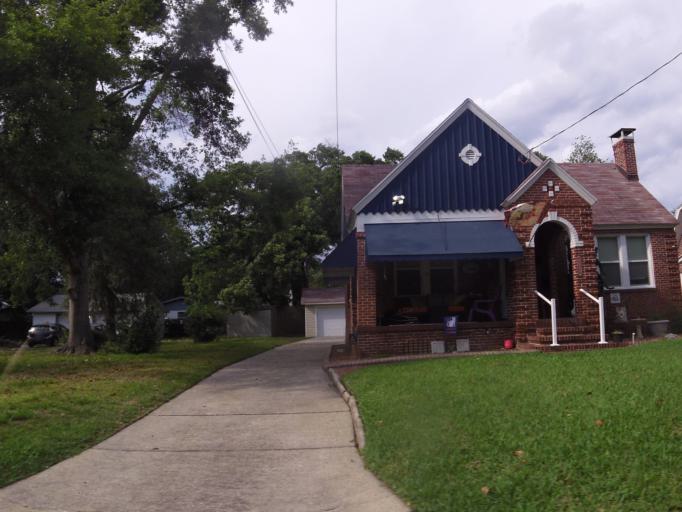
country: US
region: Florida
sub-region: Duval County
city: Jacksonville
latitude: 30.3106
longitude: -81.7256
